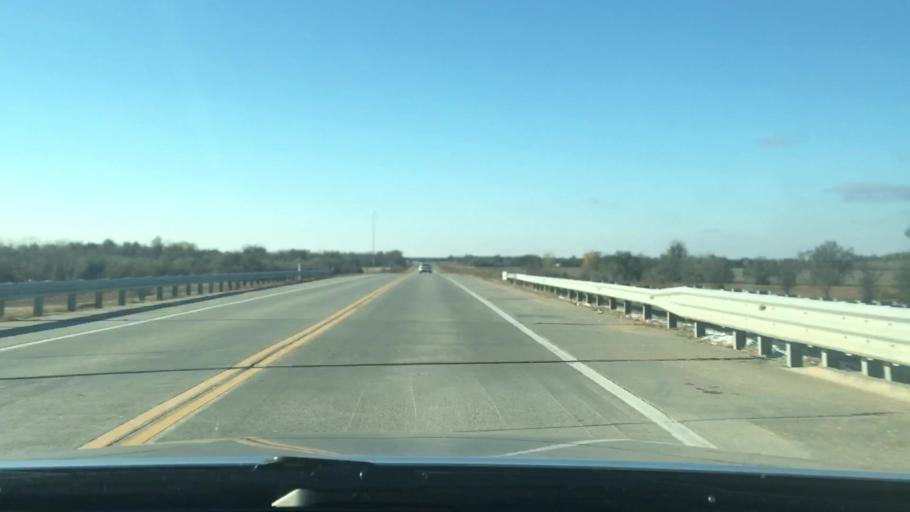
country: US
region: Kansas
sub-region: Reno County
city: Hutchinson
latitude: 38.0917
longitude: -97.9975
